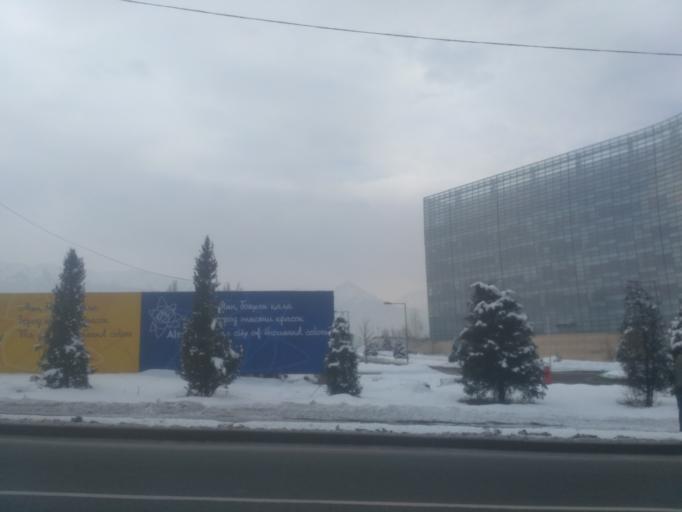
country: KZ
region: Almaty Qalasy
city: Almaty
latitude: 43.2281
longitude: 76.9453
